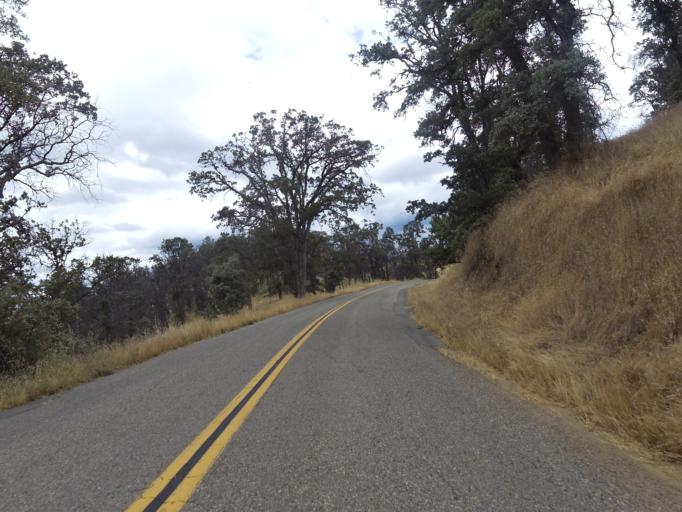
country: US
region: California
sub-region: Madera County
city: Ahwahnee
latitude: 37.3263
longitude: -119.7727
